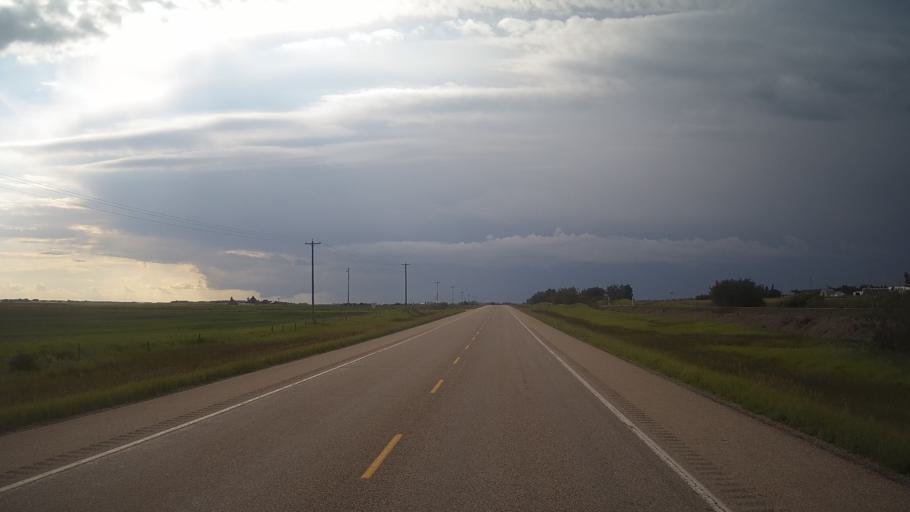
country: CA
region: Alberta
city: Vegreville
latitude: 53.2176
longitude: -112.1940
